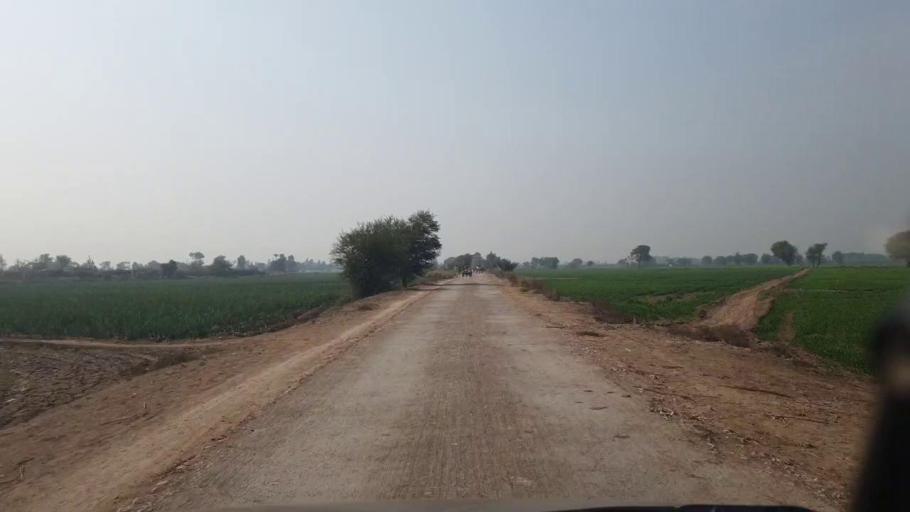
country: PK
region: Sindh
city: Shahdadpur
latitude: 26.0189
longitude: 68.5340
